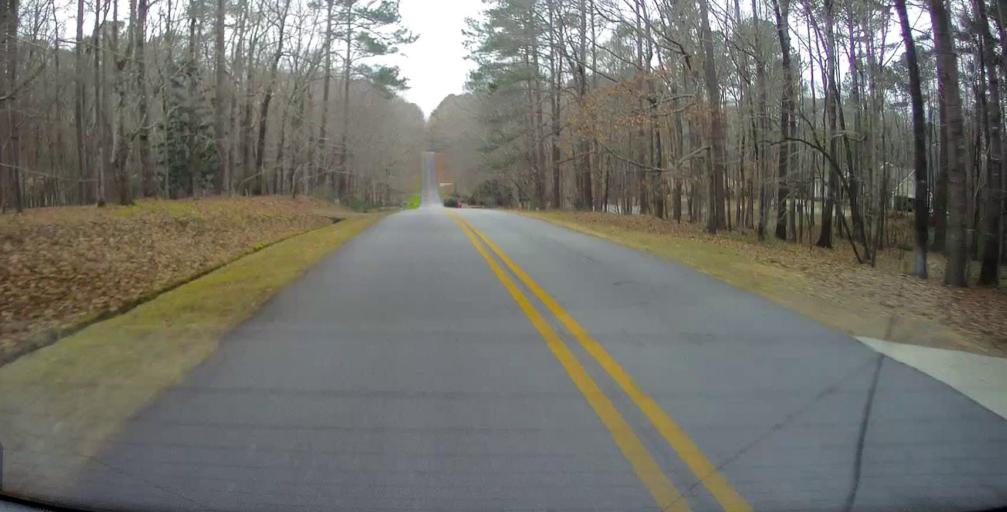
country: US
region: Georgia
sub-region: Bibb County
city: West Point
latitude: 32.9146
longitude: -83.7471
